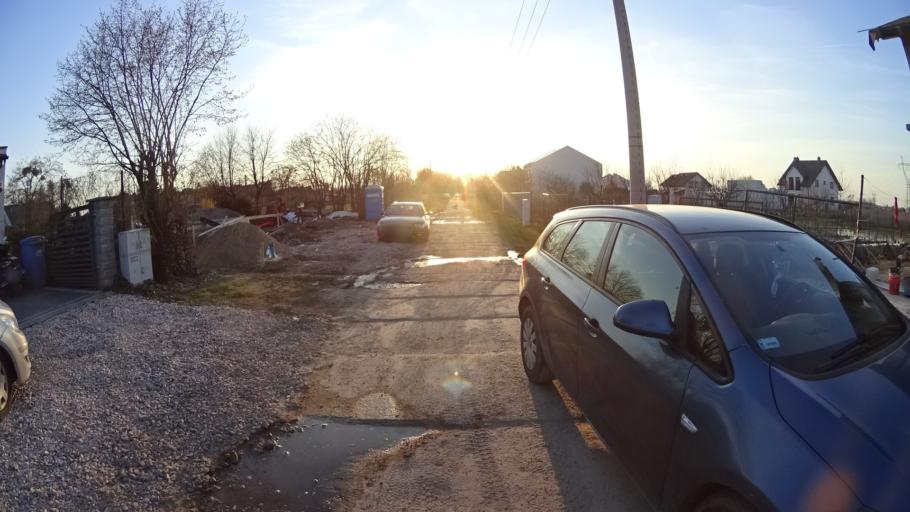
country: PL
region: Masovian Voivodeship
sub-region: Powiat warszawski zachodni
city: Stare Babice
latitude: 52.2322
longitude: 20.8208
